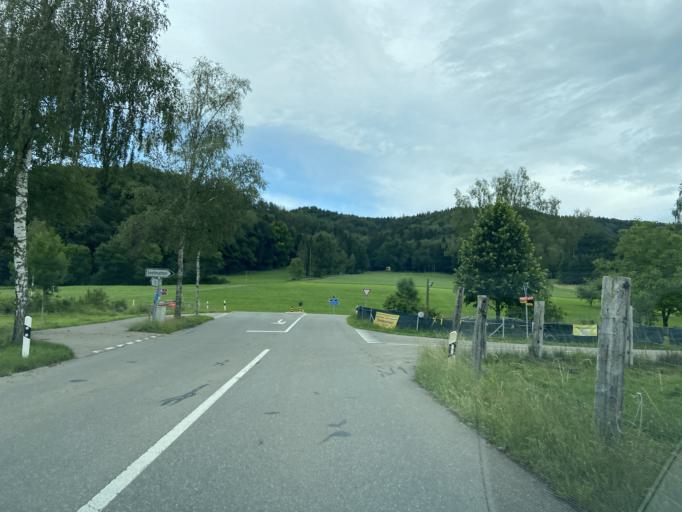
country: CH
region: Thurgau
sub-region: Muenchwilen District
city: Aadorf
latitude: 47.4548
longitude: 8.8956
